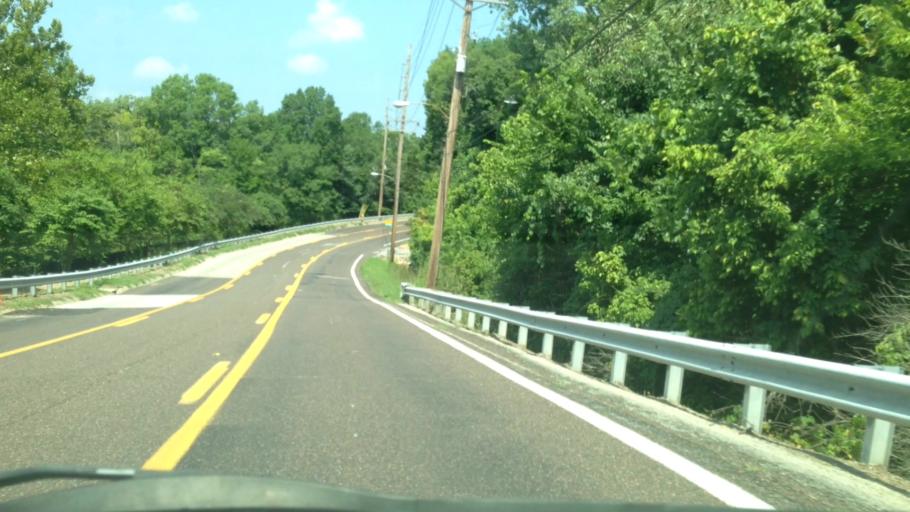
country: US
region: Missouri
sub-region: Saint Louis County
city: Des Peres
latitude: 38.5857
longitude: -90.4442
